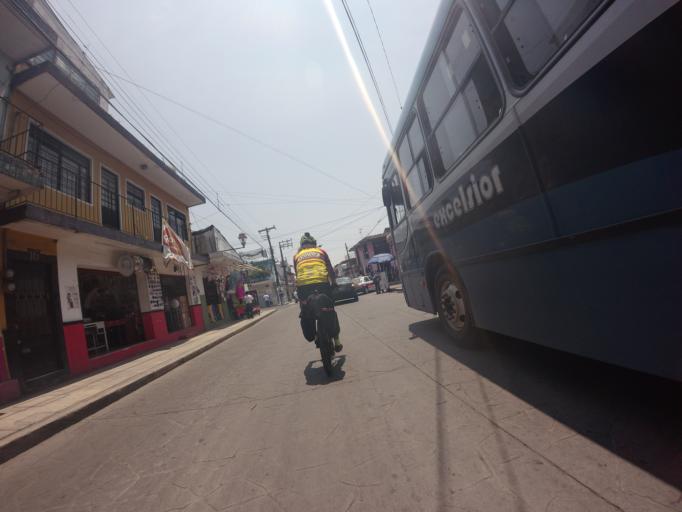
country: MX
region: Veracruz
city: Coatepec
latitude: 19.4528
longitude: -96.9616
